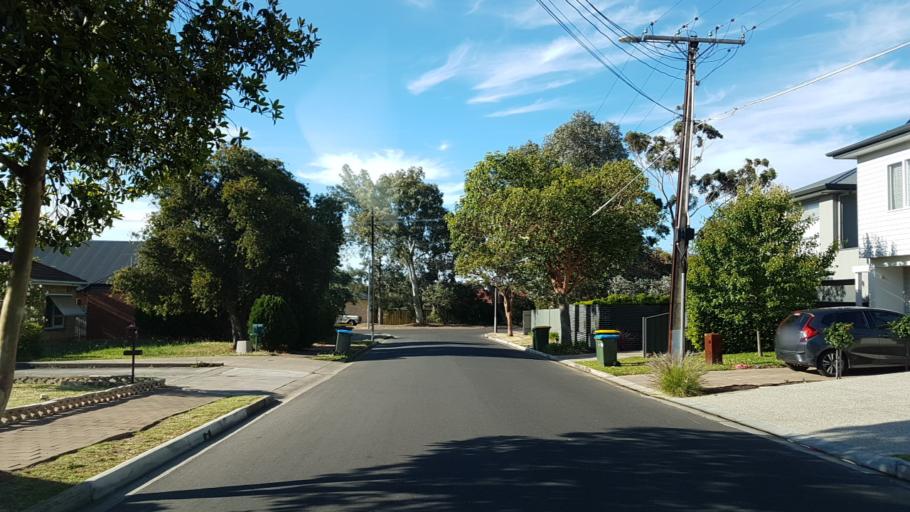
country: AU
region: South Australia
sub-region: Campbelltown
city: Campbelltown
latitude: -34.8952
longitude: 138.6800
